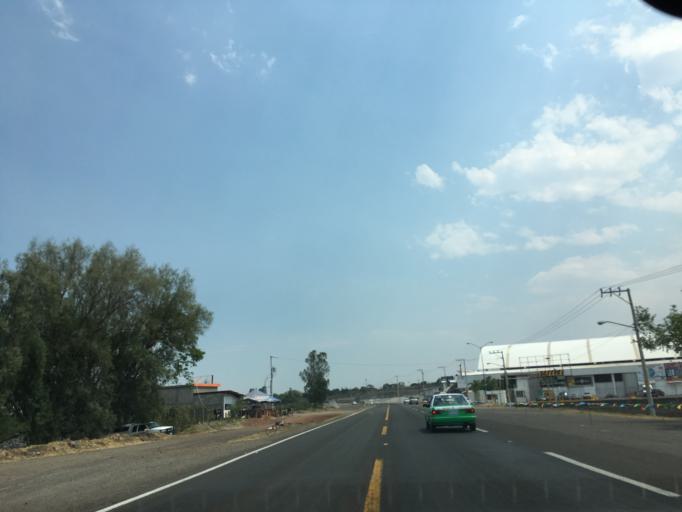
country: MX
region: Michoacan
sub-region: Cuitzeo
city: Cuamio
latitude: 20.0720
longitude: -101.1556
